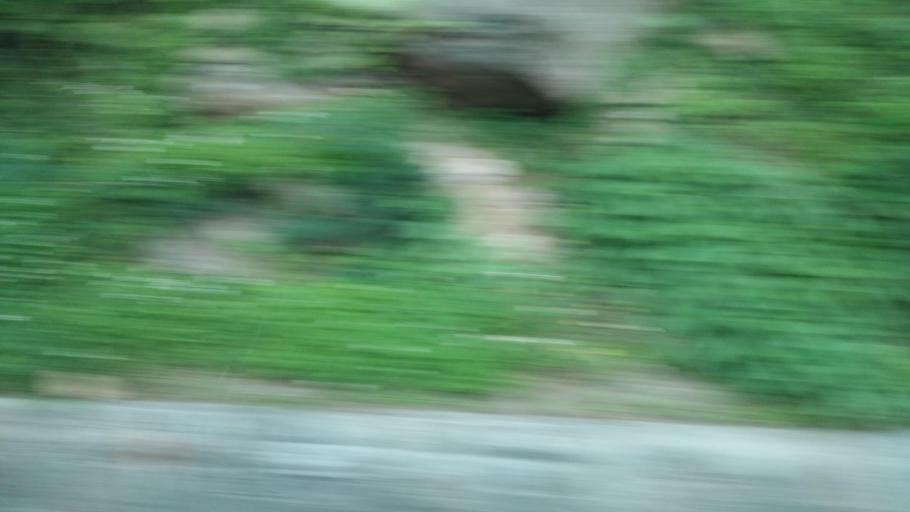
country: TW
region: Taiwan
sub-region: Hualien
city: Hualian
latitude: 24.2367
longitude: 121.7090
